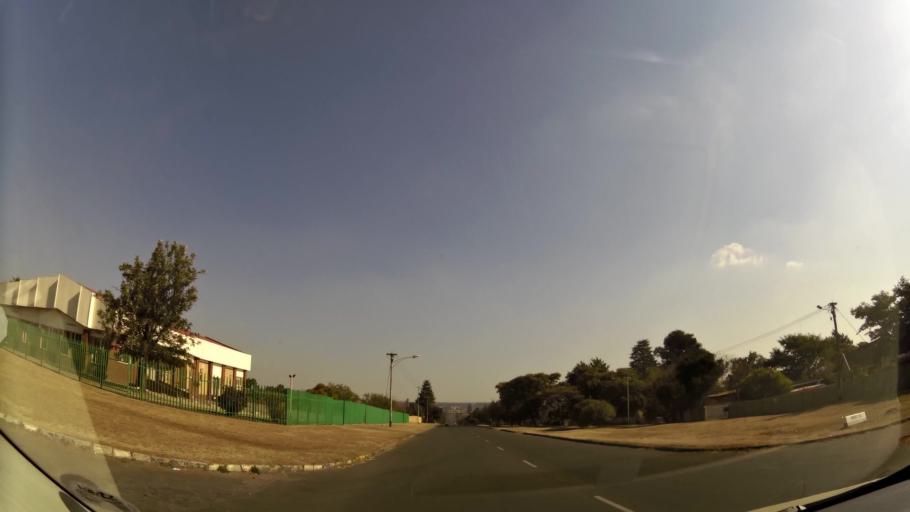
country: ZA
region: Gauteng
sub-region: West Rand District Municipality
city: Randfontein
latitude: -26.1563
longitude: 27.6987
